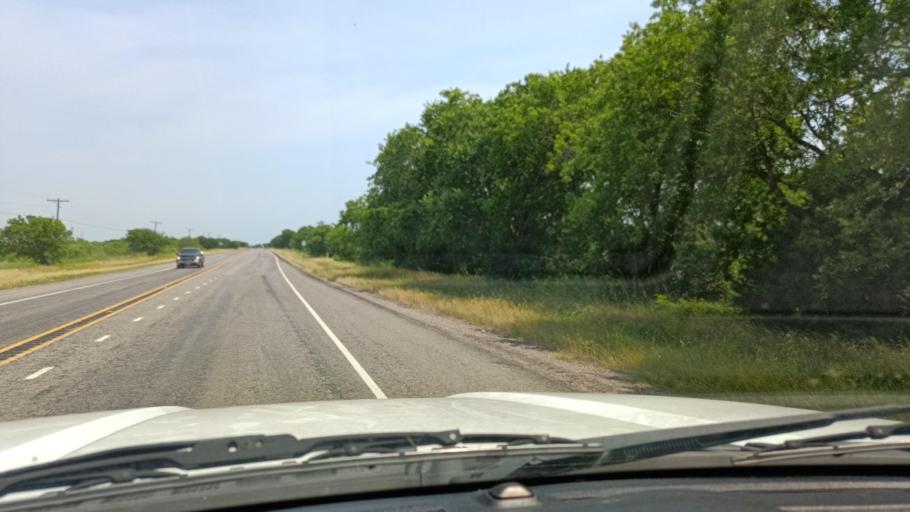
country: US
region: Texas
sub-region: Bell County
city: Rogers
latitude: 30.8683
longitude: -97.1186
